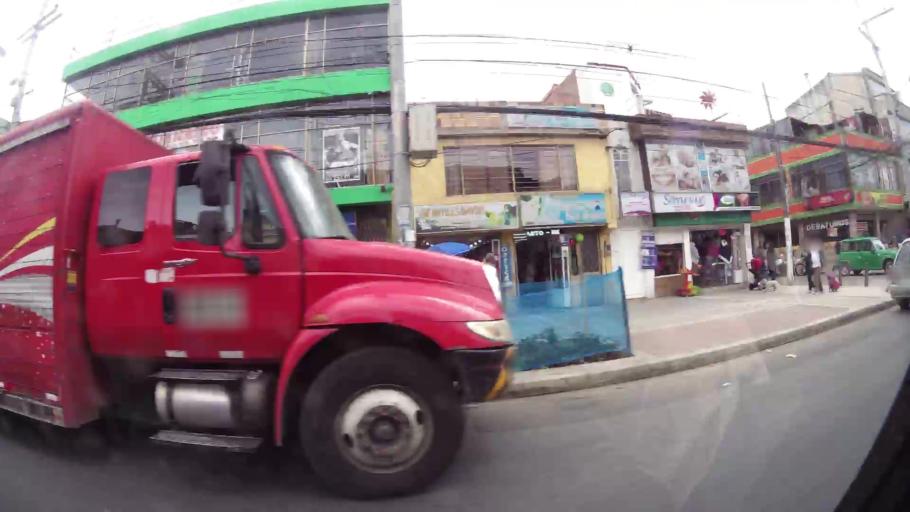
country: CO
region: Cundinamarca
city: Funza
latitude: 4.7118
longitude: -74.1404
